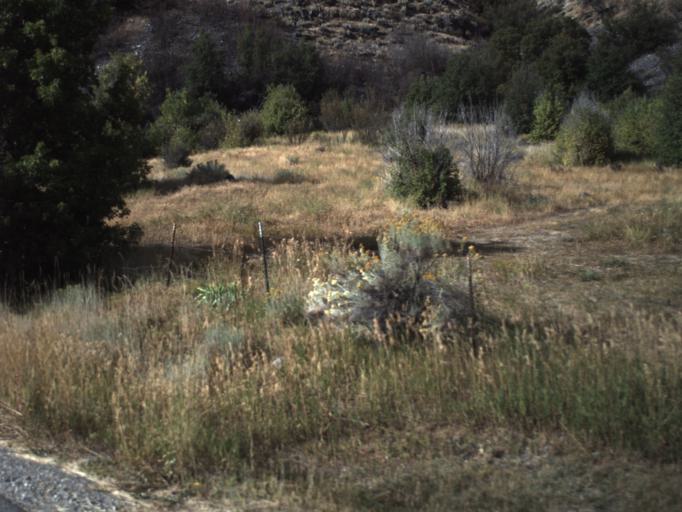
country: US
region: Utah
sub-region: Cache County
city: Millville
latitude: 41.6192
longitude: -111.6502
